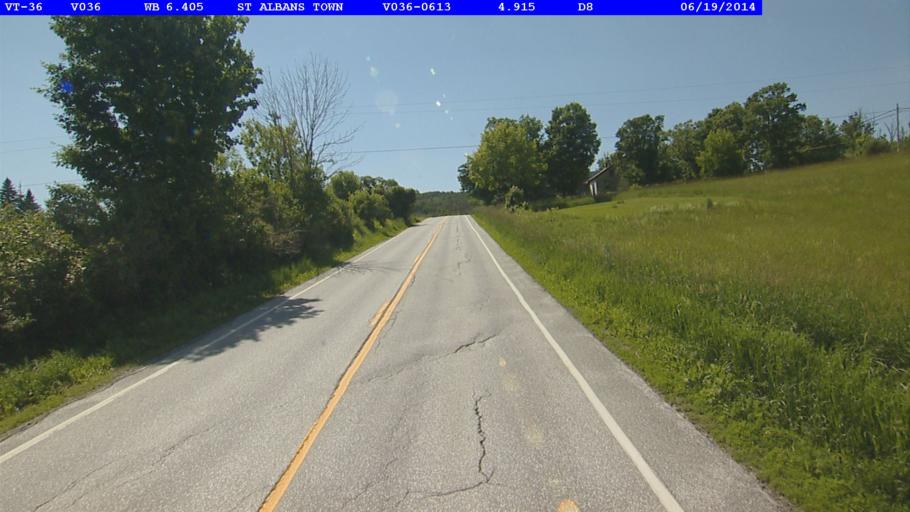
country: US
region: Vermont
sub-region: Franklin County
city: Saint Albans
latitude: 44.7903
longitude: -73.0380
